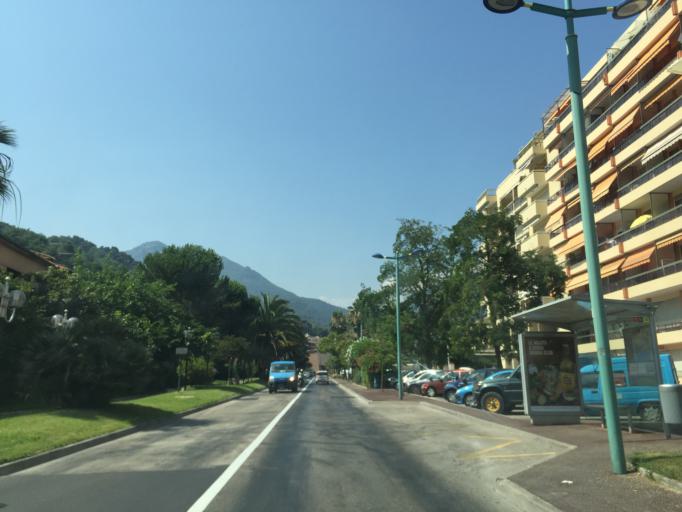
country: FR
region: Provence-Alpes-Cote d'Azur
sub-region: Departement des Alpes-Maritimes
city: Menton
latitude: 43.7864
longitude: 7.4942
